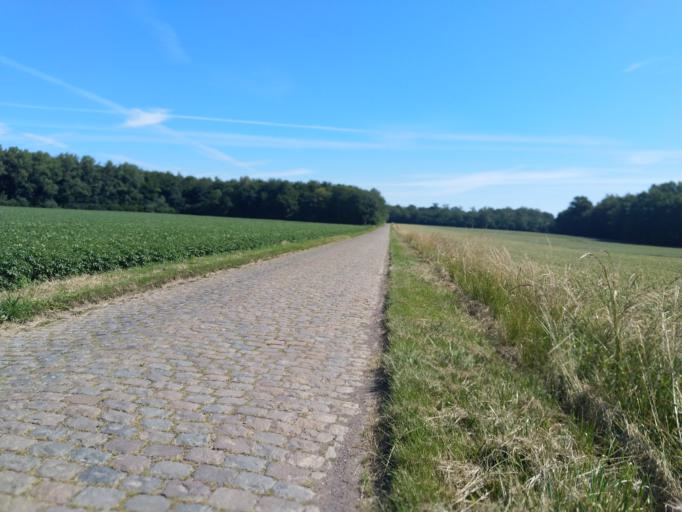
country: FR
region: Nord-Pas-de-Calais
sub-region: Departement du Nord
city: La Longueville
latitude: 50.3493
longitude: 3.8591
